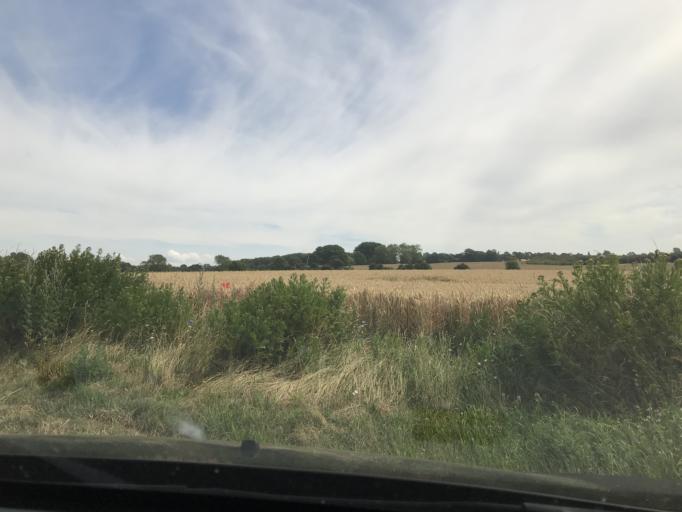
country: DK
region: South Denmark
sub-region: AEro Kommune
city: AEroskobing
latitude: 54.9098
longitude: 10.2781
